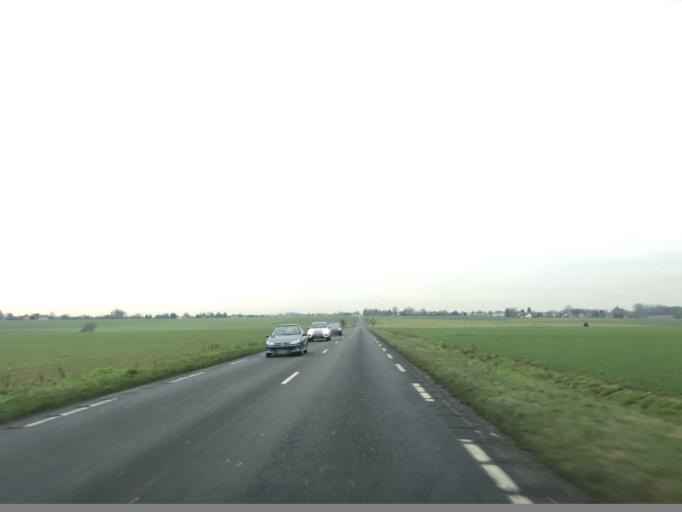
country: FR
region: Haute-Normandie
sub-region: Departement de la Seine-Maritime
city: Montmain
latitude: 49.3859
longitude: 1.2427
